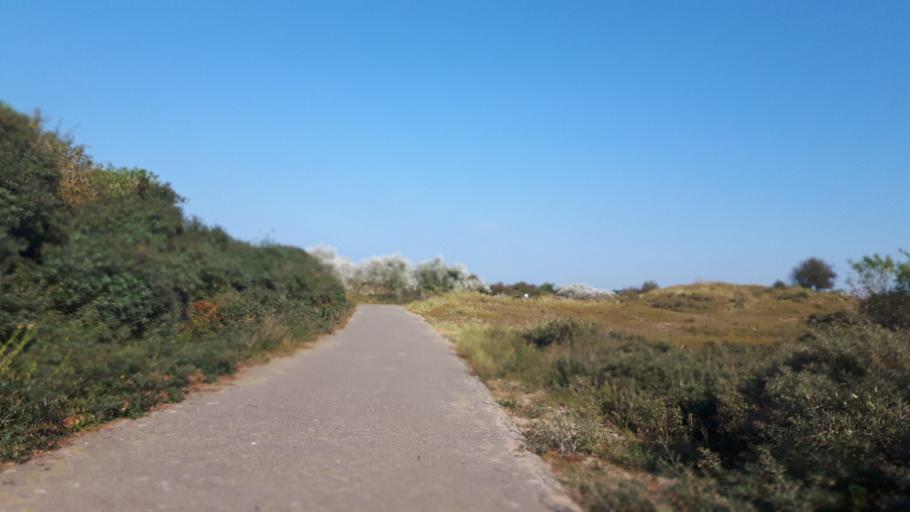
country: NL
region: North Holland
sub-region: Gemeente Zandvoort
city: Zandvoort
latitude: 52.3802
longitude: 4.5583
